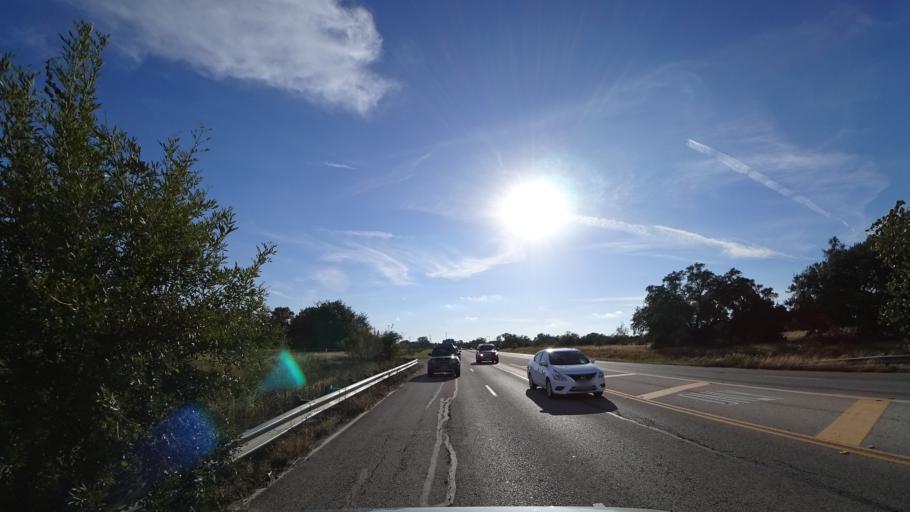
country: US
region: Texas
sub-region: Travis County
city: Wells Branch
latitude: 30.4538
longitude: -97.7236
